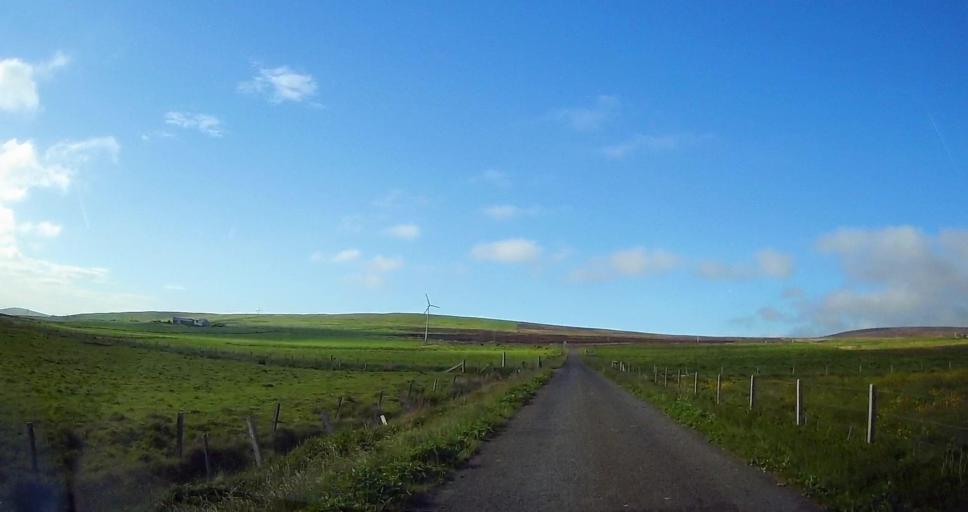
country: GB
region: Scotland
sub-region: Orkney Islands
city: Stromness
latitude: 59.0909
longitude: -3.1833
